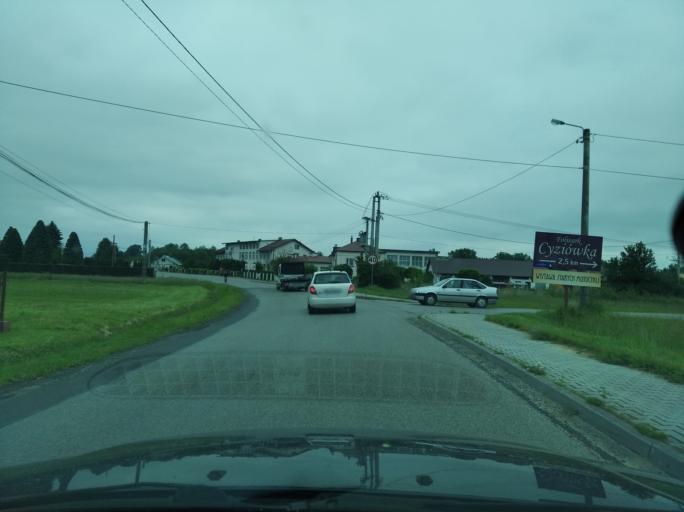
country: PL
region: Subcarpathian Voivodeship
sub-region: Powiat kolbuszowski
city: Niwiska
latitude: 50.1538
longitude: 21.6709
